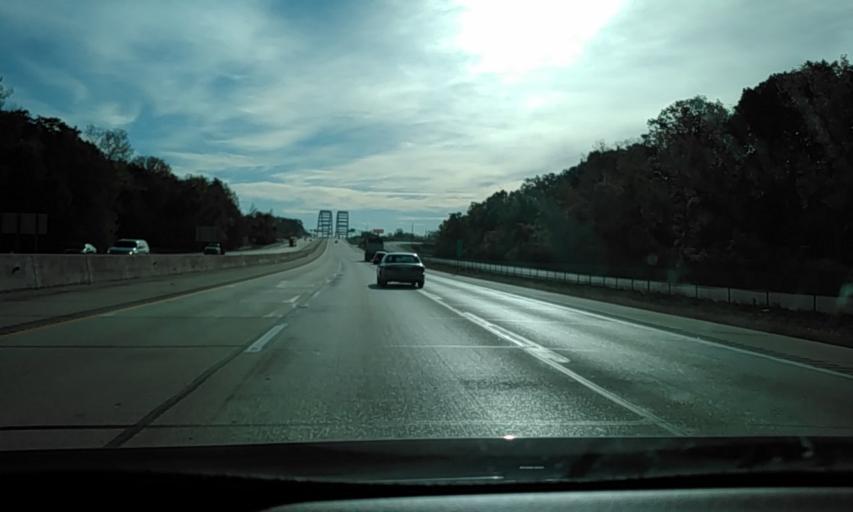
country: US
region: Missouri
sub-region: Saint Louis County
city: Oakville
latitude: 38.4912
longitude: -90.2923
